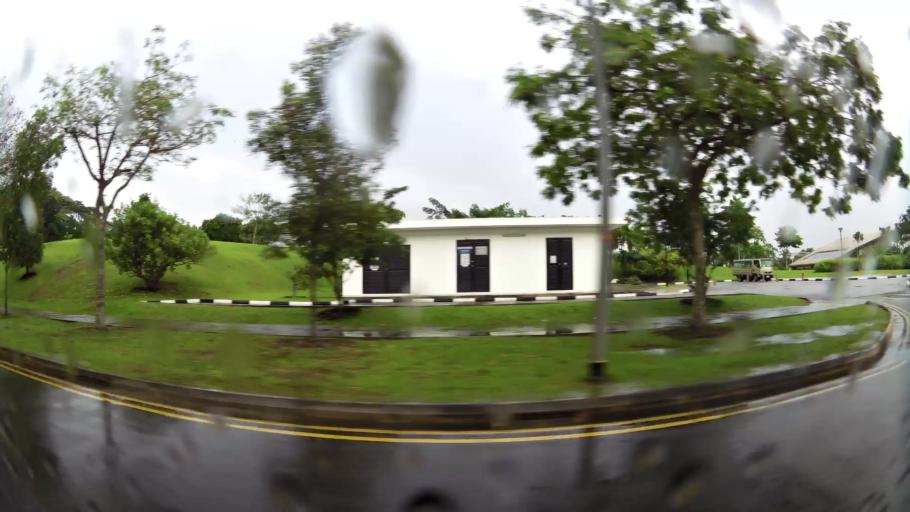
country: MY
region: Johor
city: Kampung Pasir Gudang Baru
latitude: 1.3980
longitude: 103.8834
